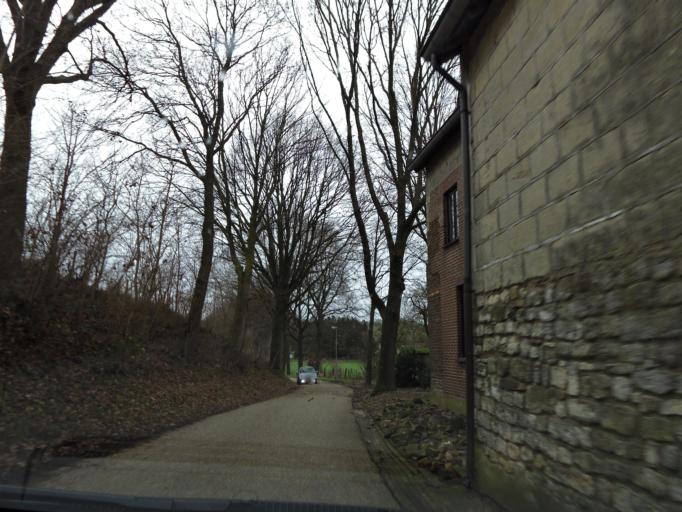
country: NL
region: Limburg
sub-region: Valkenburg aan de Geul
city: Schin op Geul
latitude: 50.8573
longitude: 5.8815
